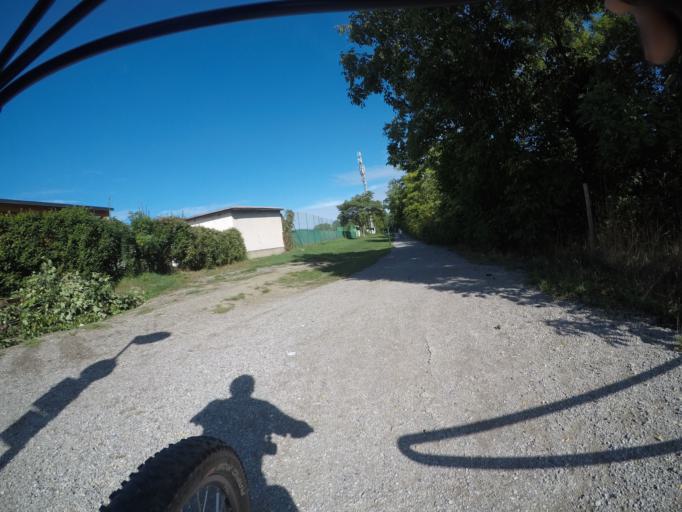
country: AT
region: Lower Austria
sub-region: Politischer Bezirk Modling
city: Brunn am Gebirge
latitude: 48.1026
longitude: 16.2988
